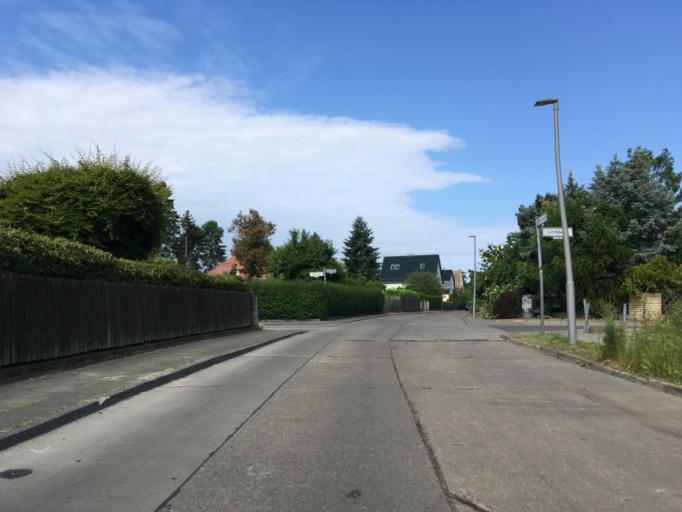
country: DE
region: Berlin
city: Friedrichsfelde
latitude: 52.5158
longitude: 13.5301
